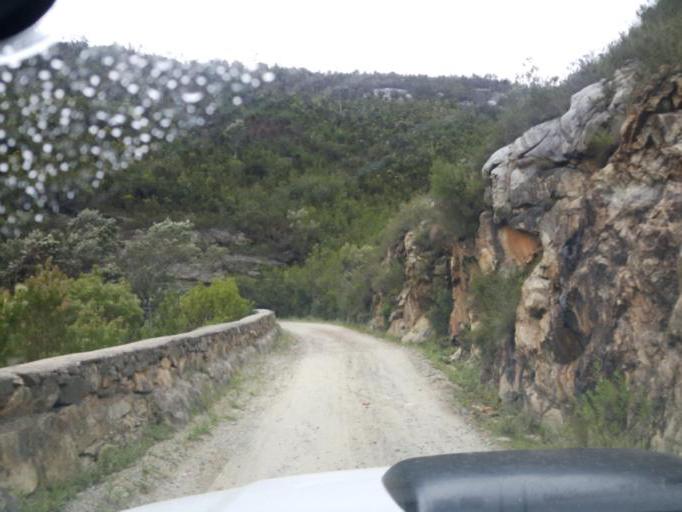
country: ZA
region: Western Cape
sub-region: Eden District Municipality
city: George
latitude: -33.8902
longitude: 22.4286
